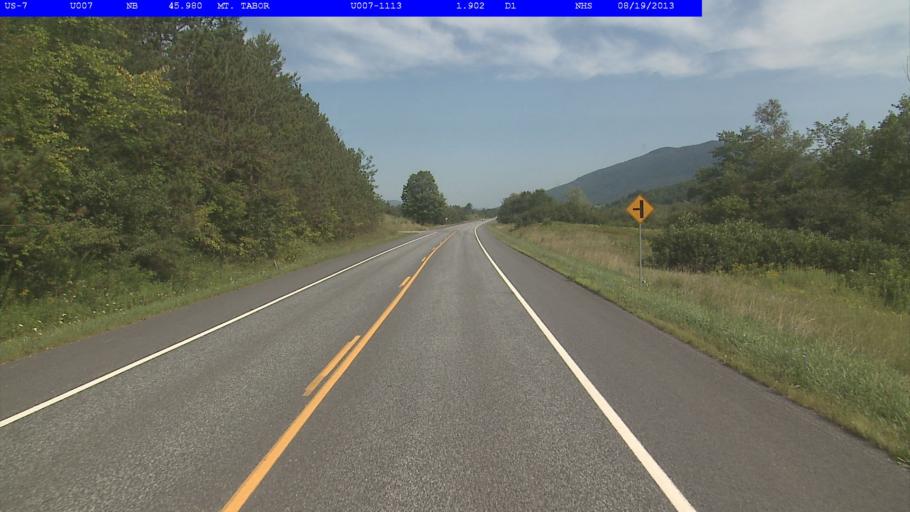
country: US
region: Vermont
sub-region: Bennington County
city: Manchester Center
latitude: 43.3324
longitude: -72.9922
